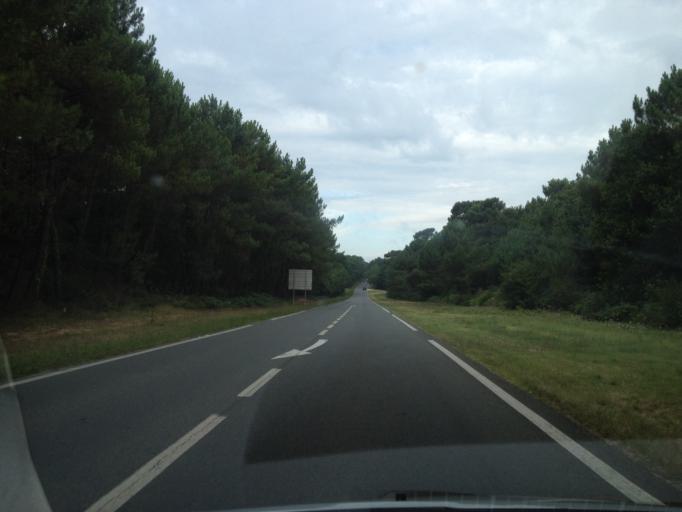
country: FR
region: Poitou-Charentes
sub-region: Departement de la Charente-Maritime
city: Saint-Palais-sur-Mer
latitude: 45.6565
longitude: -1.0923
